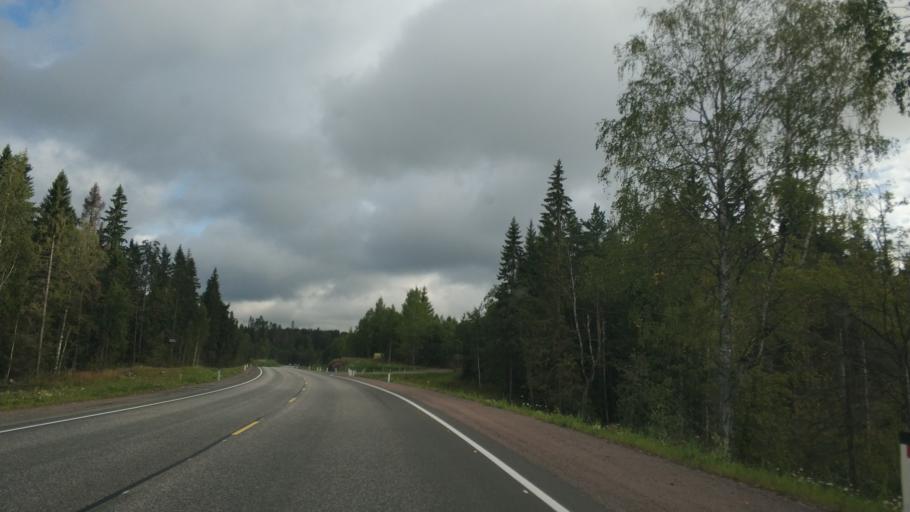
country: RU
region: Republic of Karelia
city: Khelyulya
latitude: 61.8055
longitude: 30.6197
